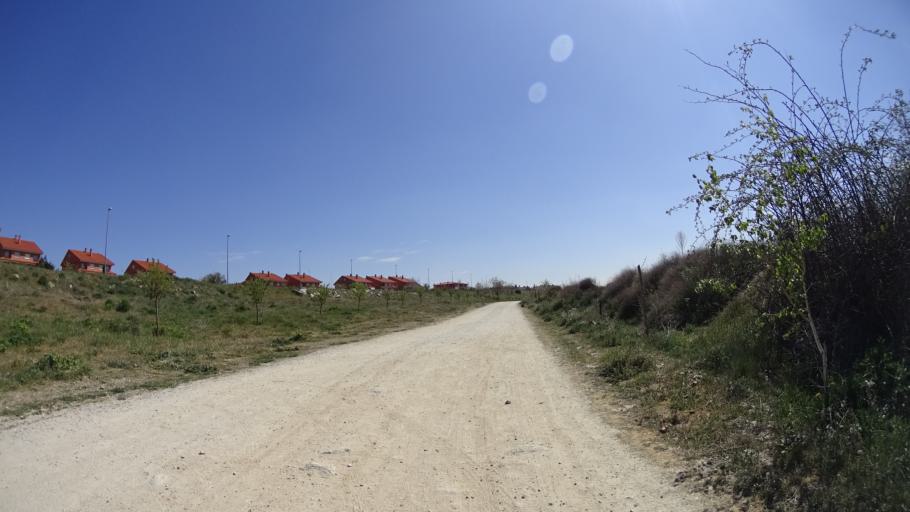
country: ES
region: Madrid
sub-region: Provincia de Madrid
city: Colmenar Viejo
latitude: 40.6692
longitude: -3.7855
